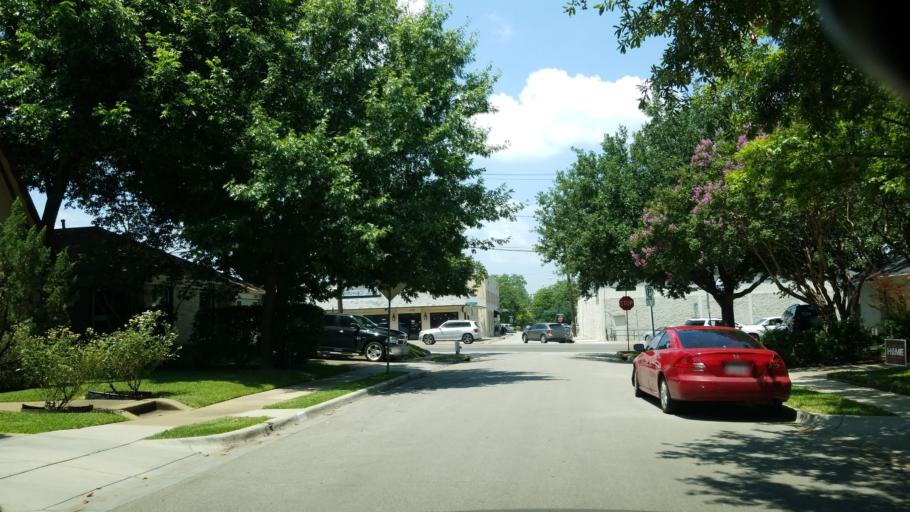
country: US
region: Texas
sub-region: Dallas County
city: University Park
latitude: 32.8503
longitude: -96.7864
